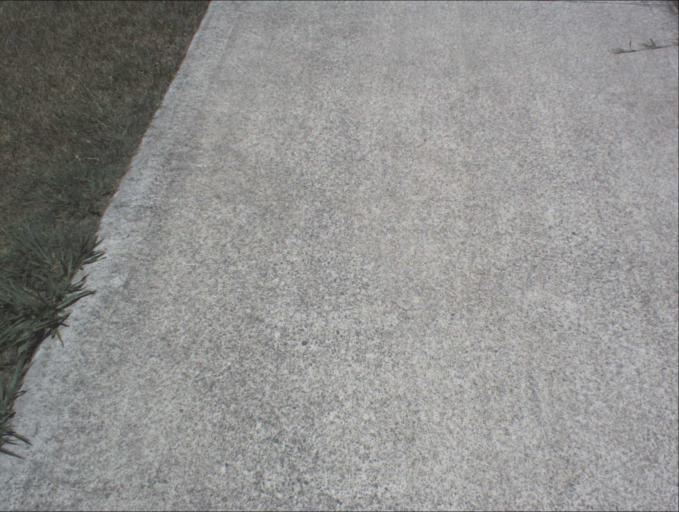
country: AU
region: Queensland
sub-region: Gold Coast
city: Yatala
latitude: -27.7192
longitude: 153.2156
